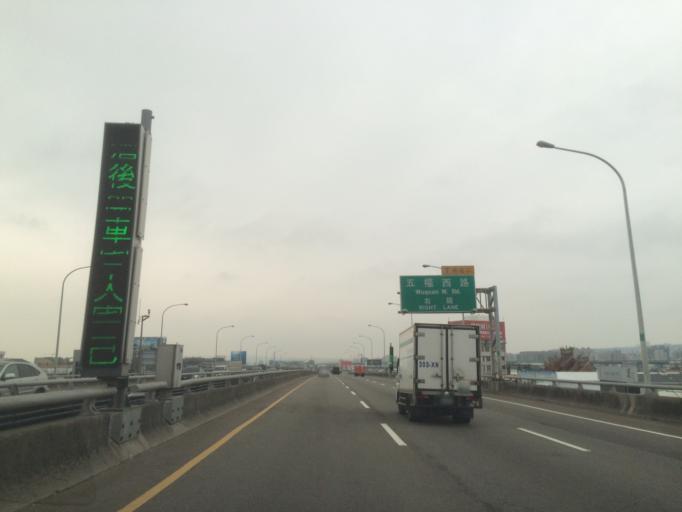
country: TW
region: Taiwan
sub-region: Taichung City
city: Taichung
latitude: 24.1621
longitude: 120.6284
